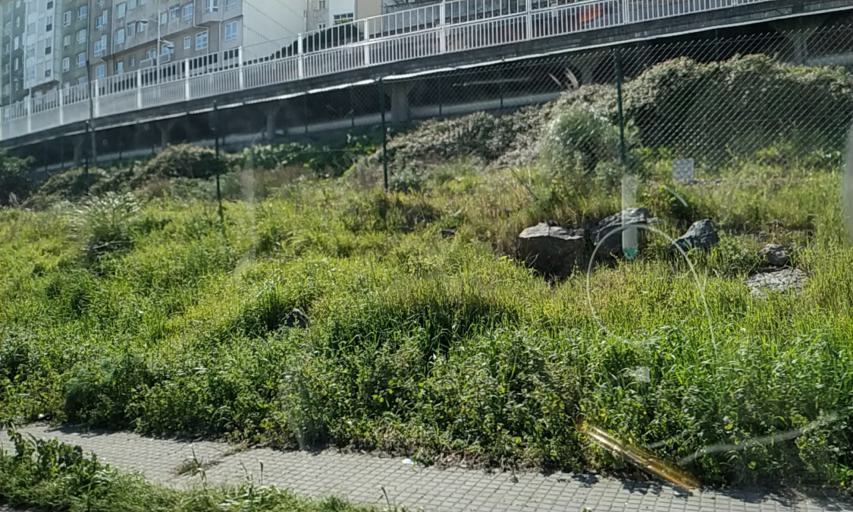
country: ES
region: Galicia
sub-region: Provincia da Coruna
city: A Coruna
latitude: 43.3533
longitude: -8.3874
